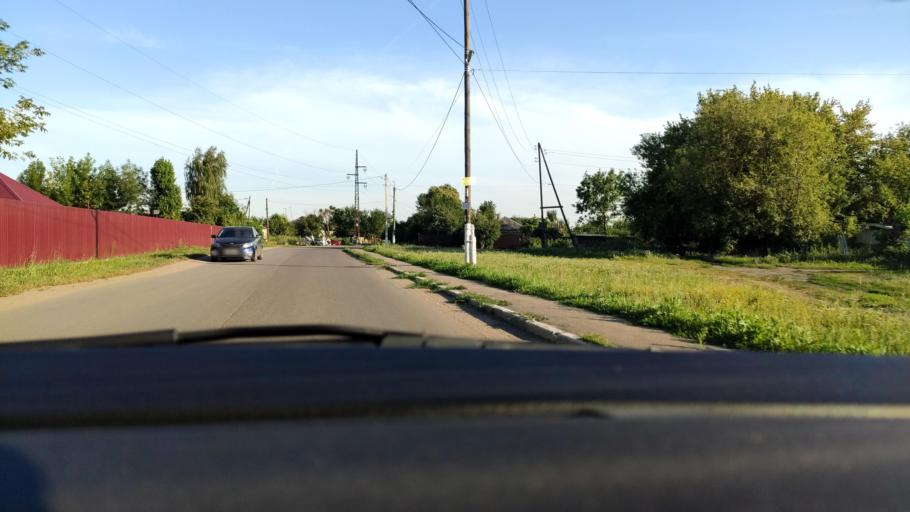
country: RU
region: Voronezj
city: Latnaya
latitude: 51.6598
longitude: 38.9064
